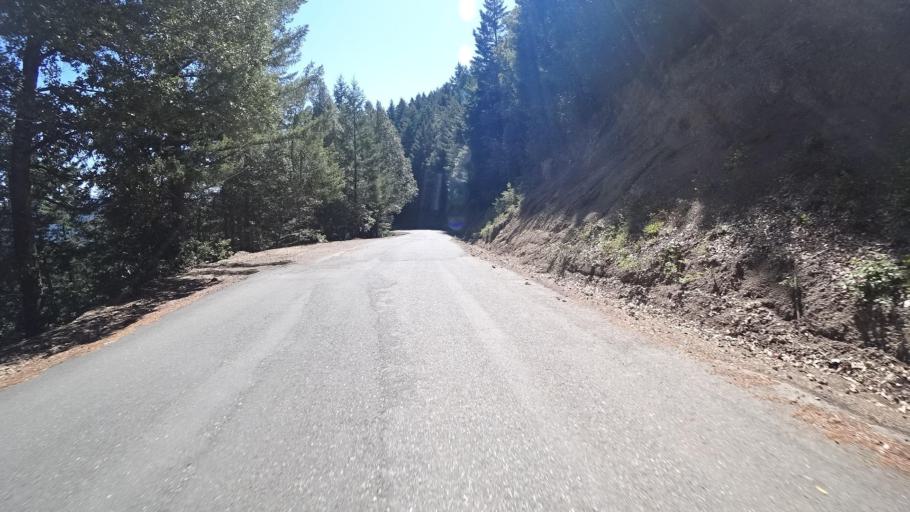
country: US
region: California
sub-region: Humboldt County
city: Redway
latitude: 40.1583
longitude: -124.0771
